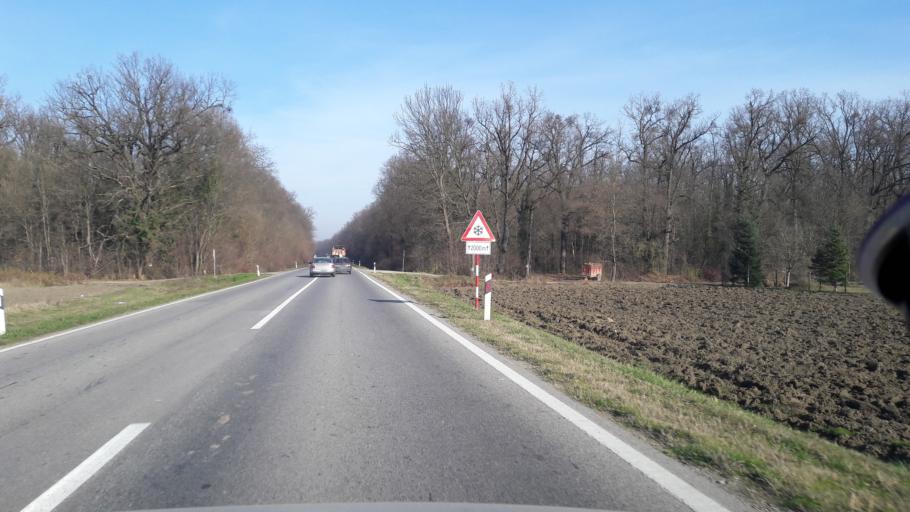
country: HR
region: Vukovarsko-Srijemska
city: Gradiste
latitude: 45.1195
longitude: 18.7091
